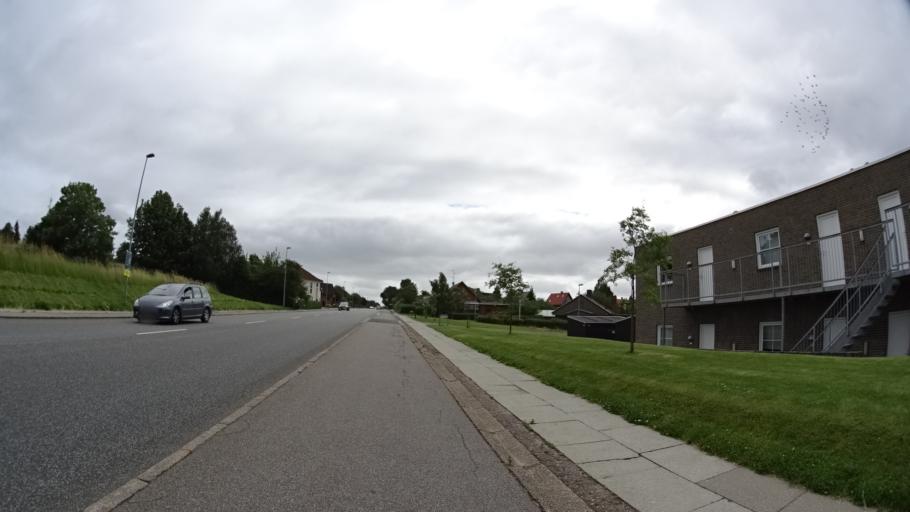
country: DK
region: Central Jutland
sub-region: Arhus Kommune
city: Arhus
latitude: 56.1273
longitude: 10.1725
